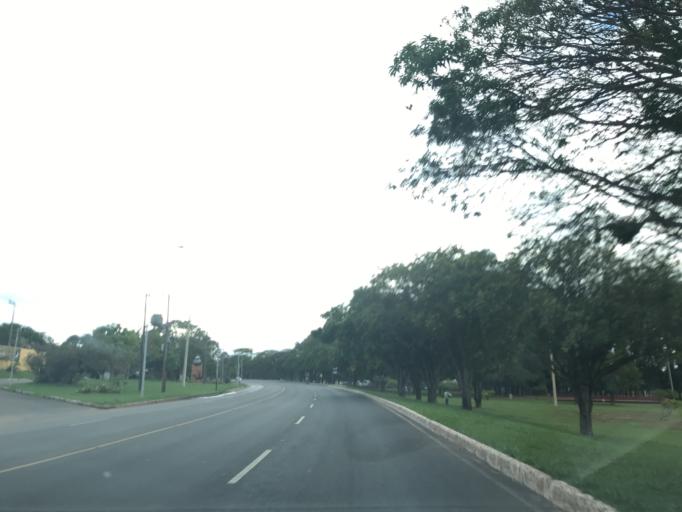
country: BR
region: Federal District
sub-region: Brasilia
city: Brasilia
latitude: -15.8052
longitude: -47.9221
